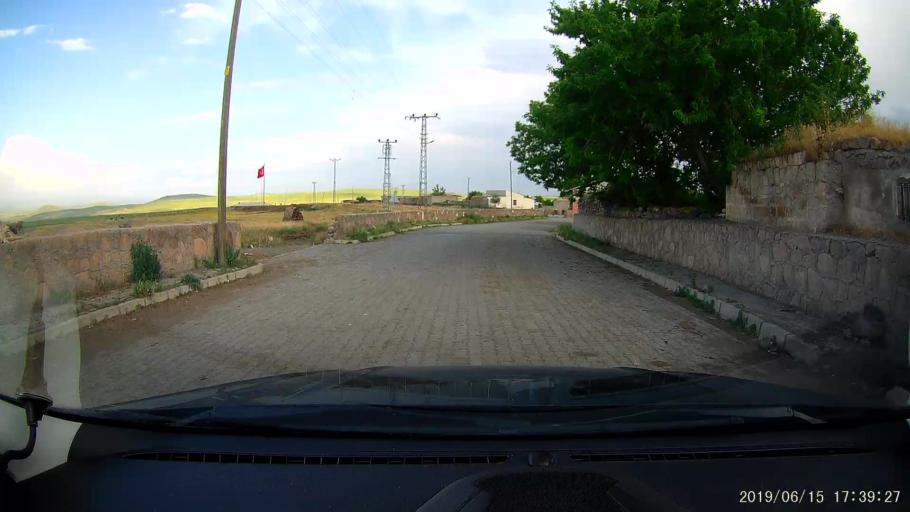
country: TR
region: Kars
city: Basgedikler
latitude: 40.5161
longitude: 43.5702
